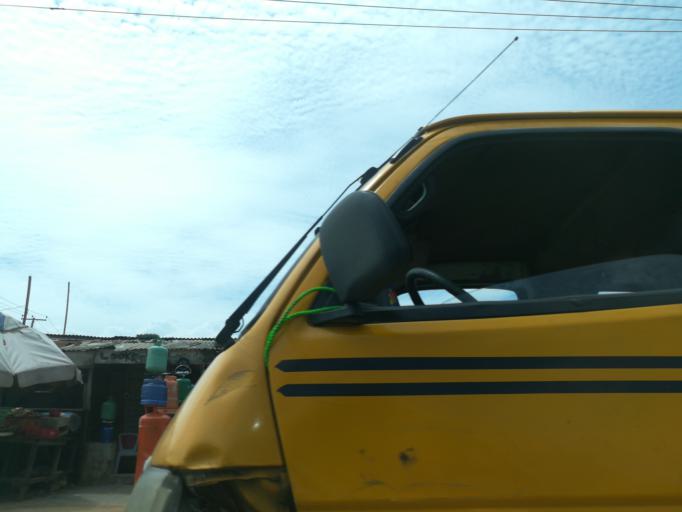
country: NG
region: Lagos
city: Ebute Ikorodu
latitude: 6.5680
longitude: 3.4794
